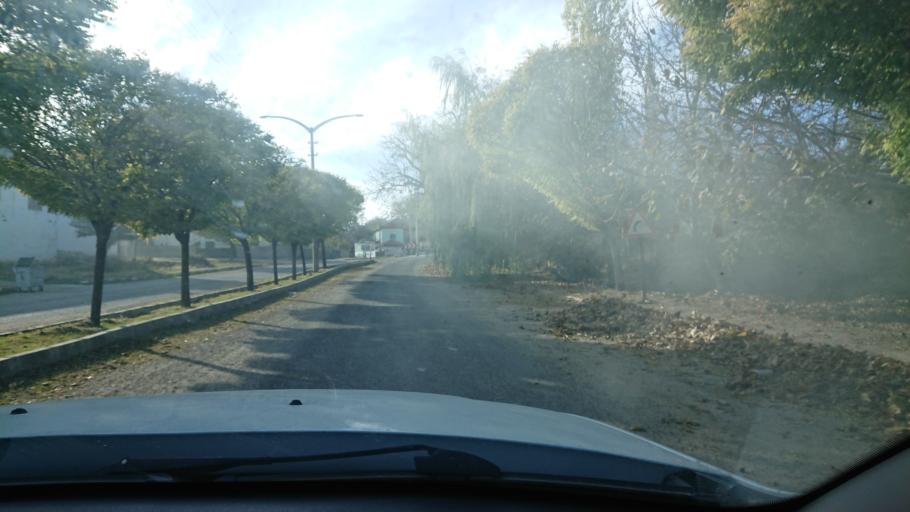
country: TR
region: Aksaray
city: Sariyahsi
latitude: 38.9593
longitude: 33.8868
